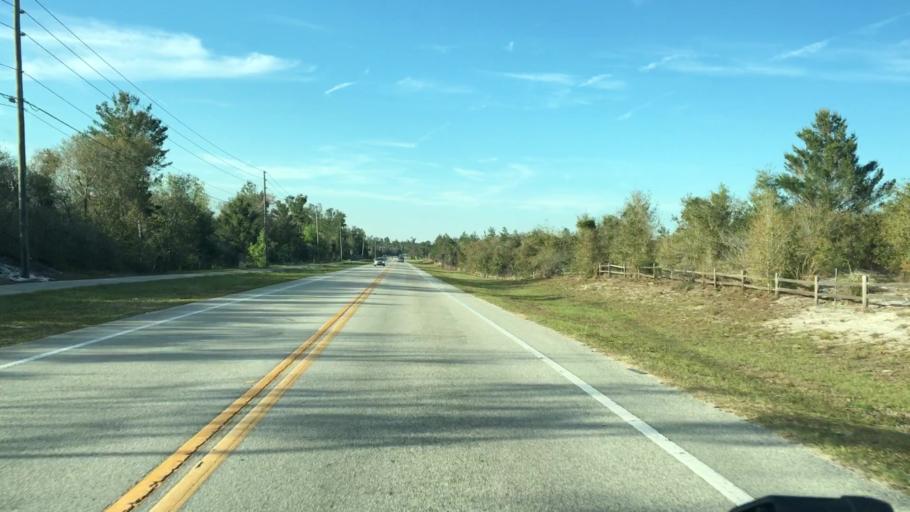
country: US
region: Florida
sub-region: Volusia County
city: Deltona
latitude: 28.9229
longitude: -81.2218
